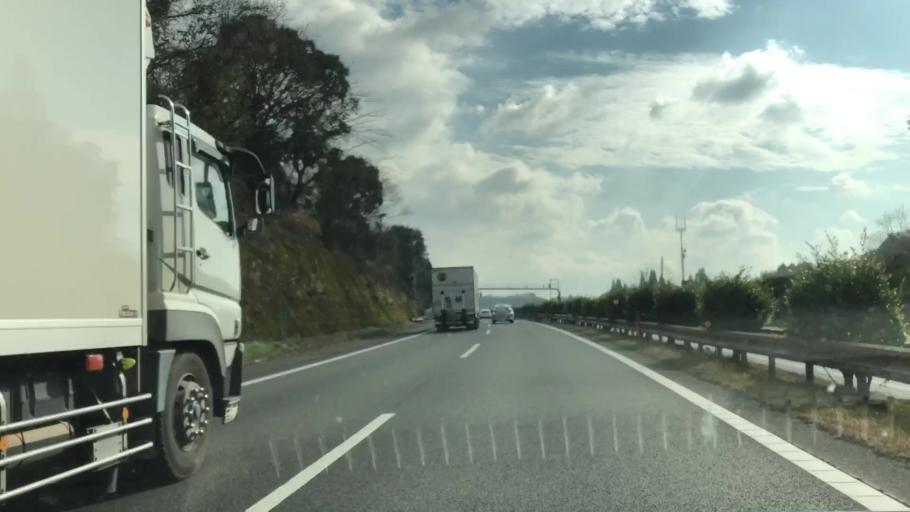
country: JP
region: Fukuoka
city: Setakamachi-takayanagi
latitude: 33.0894
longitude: 130.5393
